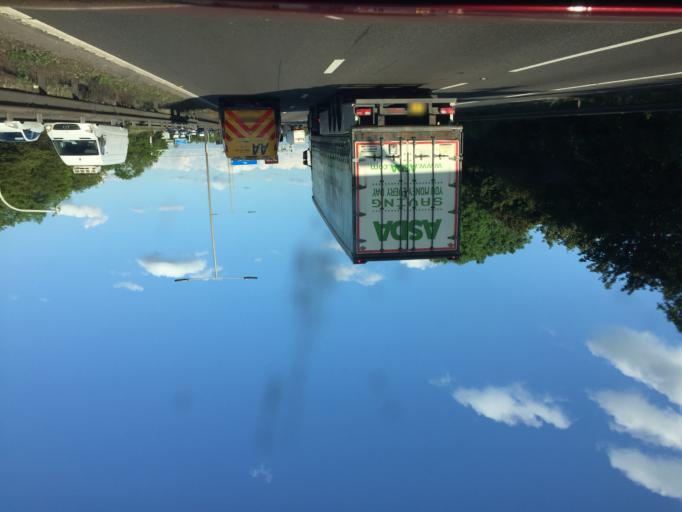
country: GB
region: England
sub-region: Warwickshire
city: Water Orton
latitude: 52.5156
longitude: -1.7716
